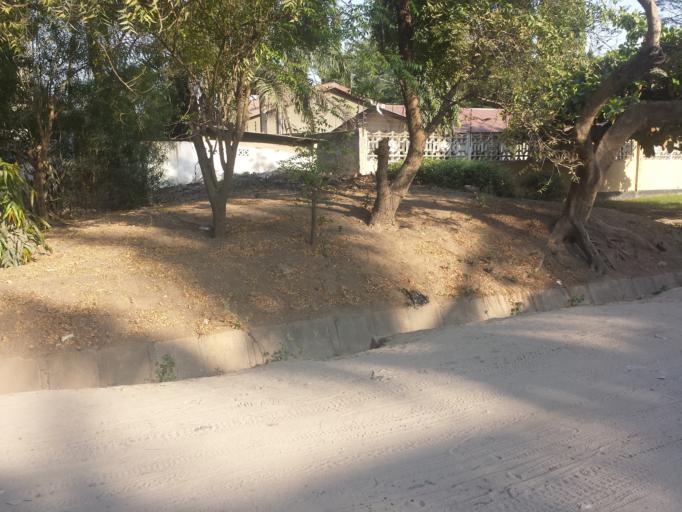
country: TZ
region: Dar es Salaam
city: Magomeni
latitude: -6.8345
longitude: 39.2212
